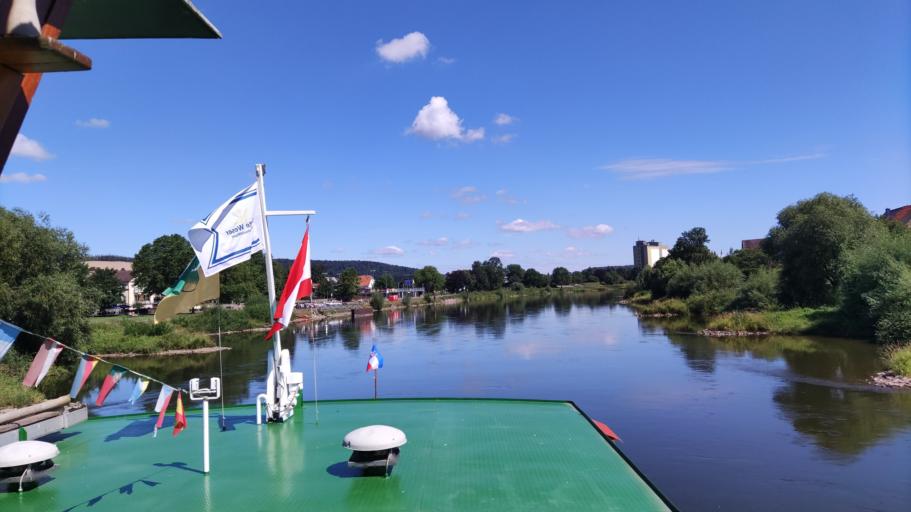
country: DE
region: North Rhine-Westphalia
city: Beverungen
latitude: 51.6623
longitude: 9.3786
